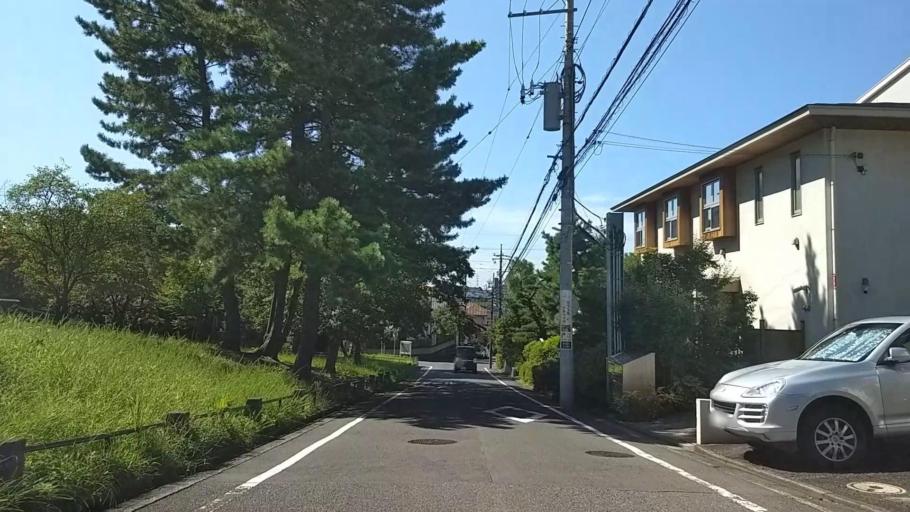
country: JP
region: Tokyo
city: Chofugaoka
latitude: 35.5737
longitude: 139.5564
